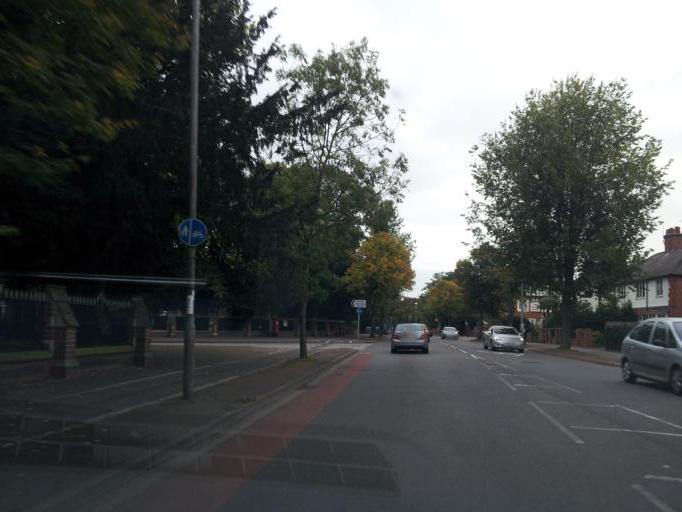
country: GB
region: England
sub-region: Nottinghamshire
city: Newark on Trent
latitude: 53.0691
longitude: -0.7984
